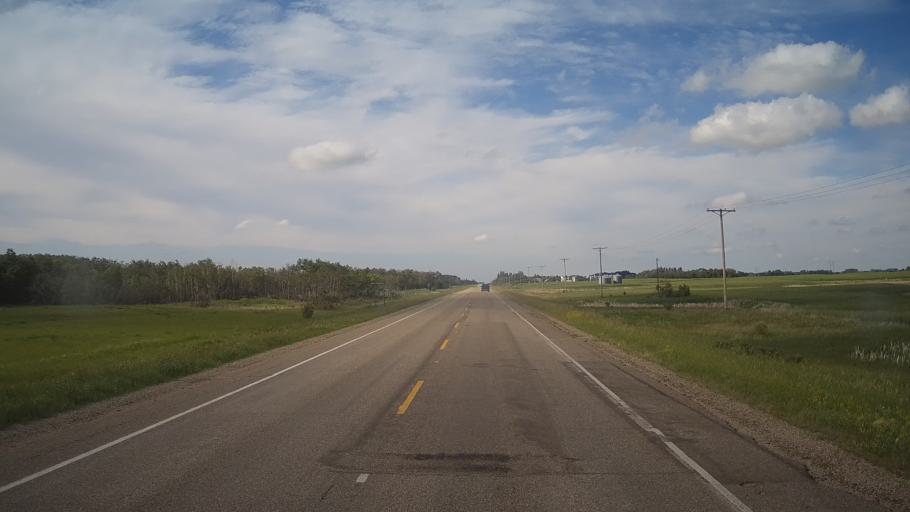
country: CA
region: Saskatchewan
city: Foam Lake
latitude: 51.5795
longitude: -103.8457
